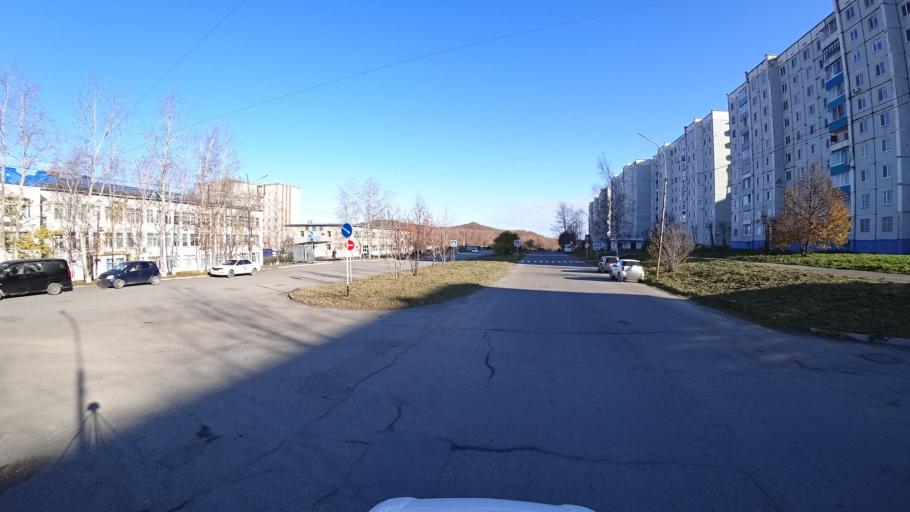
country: RU
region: Khabarovsk Krai
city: Amursk
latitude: 50.2468
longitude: 136.9164
